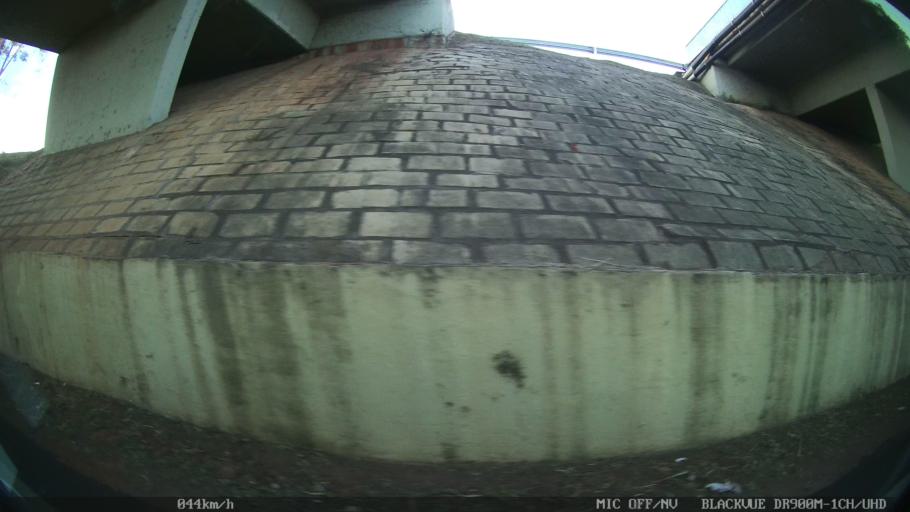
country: BR
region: Sao Paulo
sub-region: Catanduva
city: Catanduva
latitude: -21.1594
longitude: -48.9862
